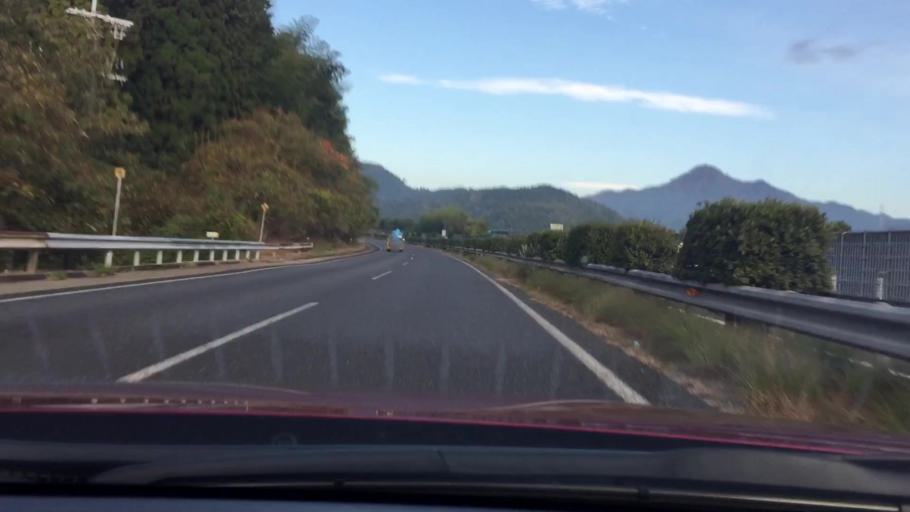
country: JP
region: Hyogo
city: Yamazakicho-nakabirose
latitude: 34.9662
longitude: 134.6771
